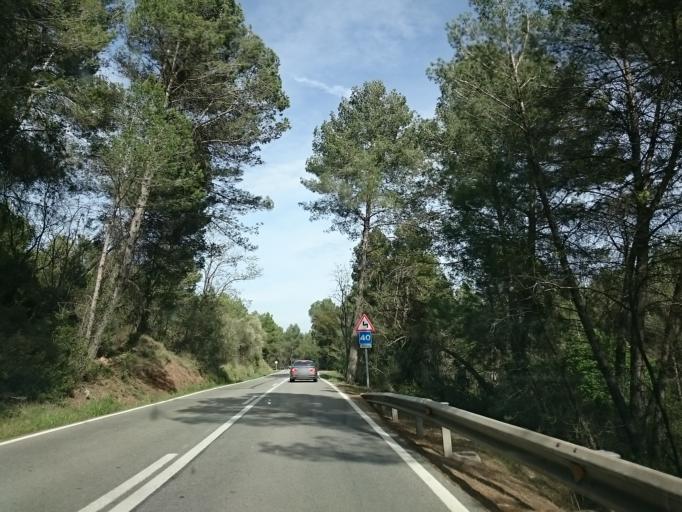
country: ES
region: Catalonia
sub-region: Provincia de Barcelona
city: Jorba
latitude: 41.5817
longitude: 1.5557
